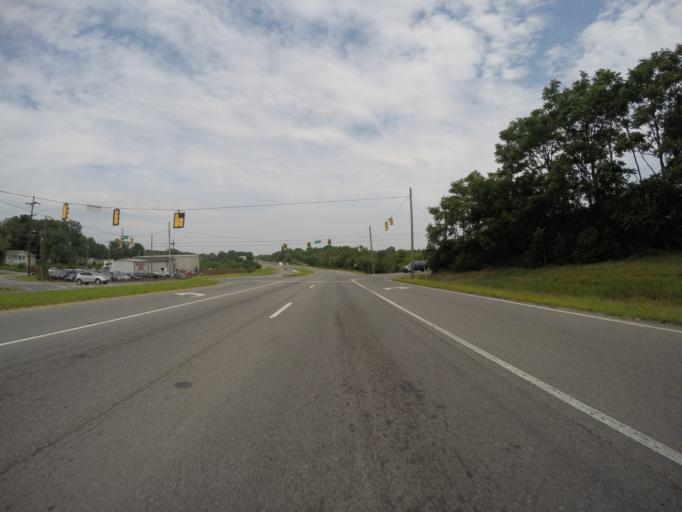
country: US
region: Tennessee
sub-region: Davidson County
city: Lakewood
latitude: 36.2629
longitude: -86.6805
